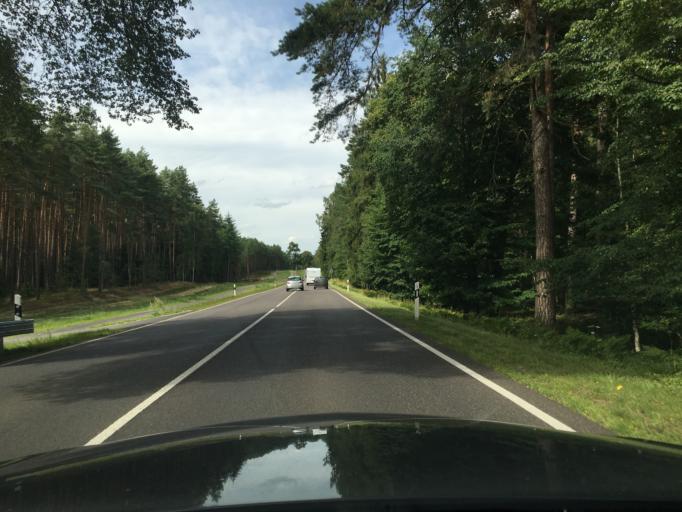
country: DE
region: Mecklenburg-Vorpommern
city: Neustrelitz
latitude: 53.2861
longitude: 13.1099
